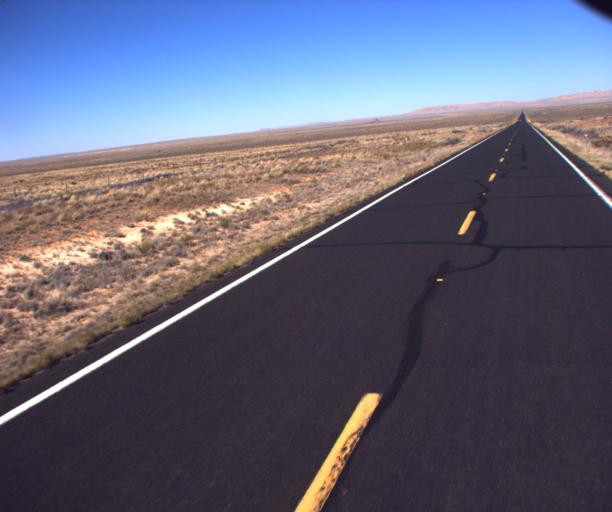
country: US
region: Arizona
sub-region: Navajo County
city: First Mesa
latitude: 35.6726
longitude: -110.4974
